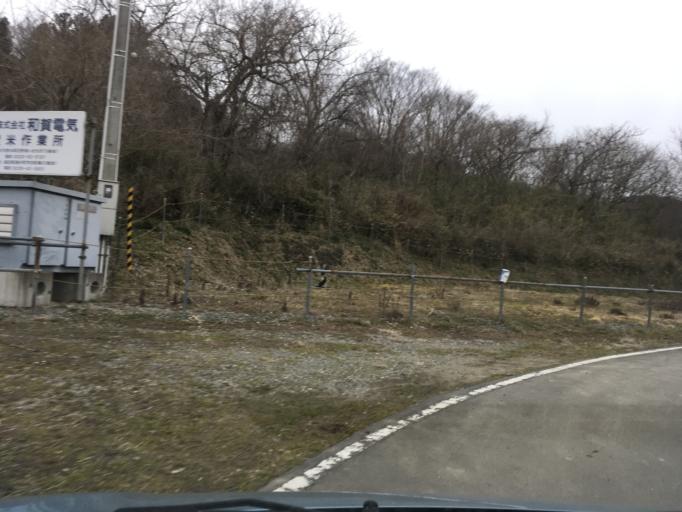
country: JP
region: Miyagi
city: Wakuya
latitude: 38.6712
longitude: 141.2715
